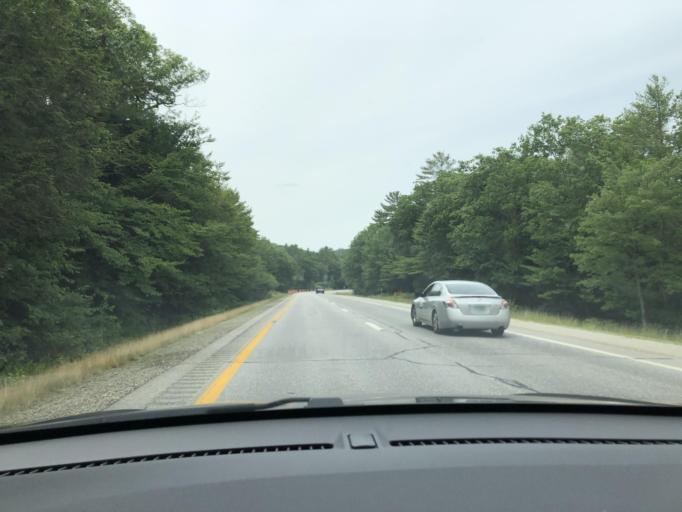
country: US
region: New Hampshire
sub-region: Merrimack County
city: Sutton
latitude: 43.3193
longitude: -71.8832
